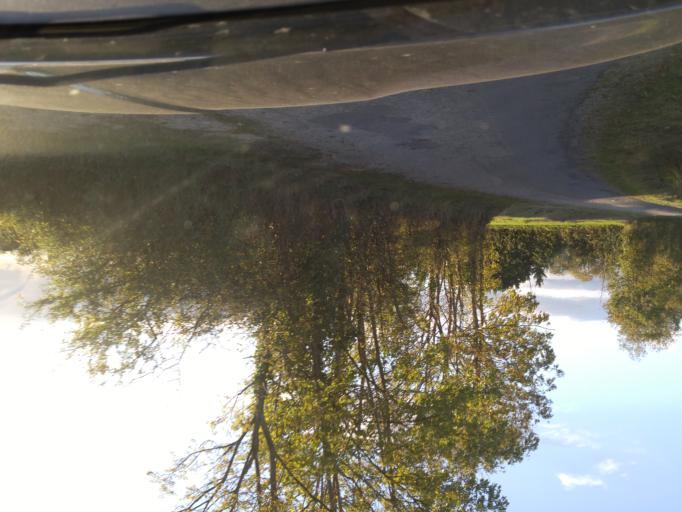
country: FR
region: Lower Normandy
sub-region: Departement de la Manche
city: Valognes
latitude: 49.5175
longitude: -1.4718
